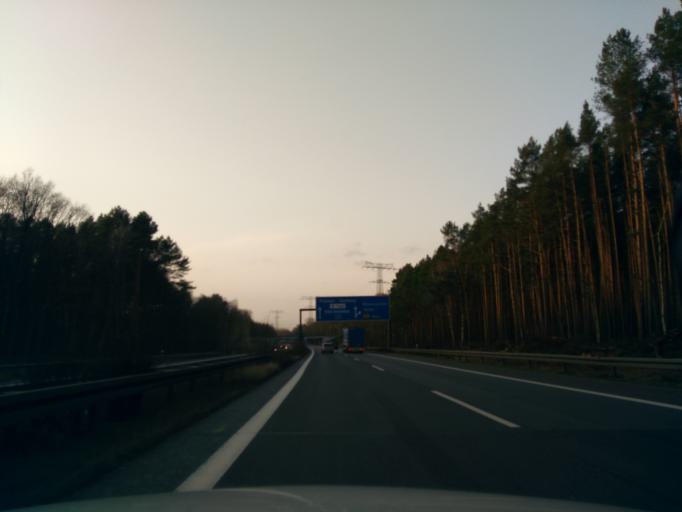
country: DE
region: Brandenburg
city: Birkenwerder
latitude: 52.6986
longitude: 13.2896
